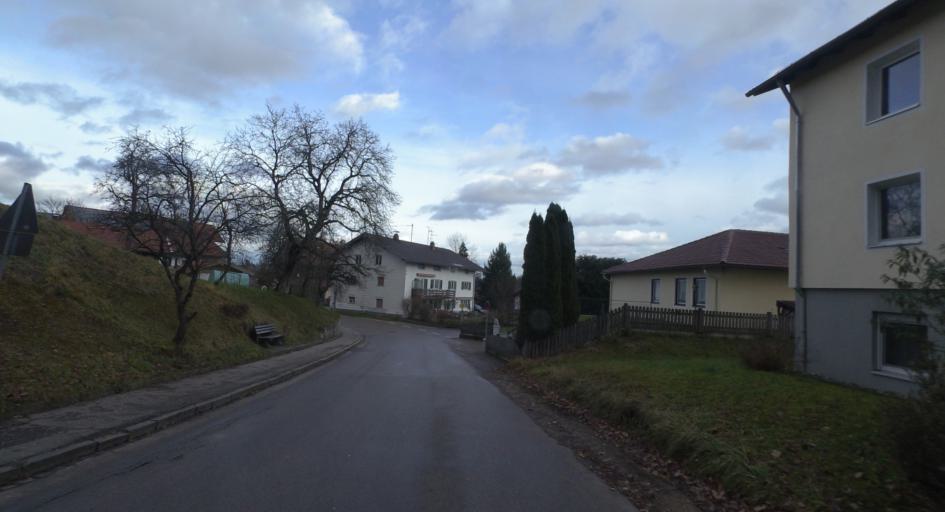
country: DE
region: Bavaria
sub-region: Upper Bavaria
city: Prien am Chiemsee
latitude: 47.8495
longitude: 12.3397
